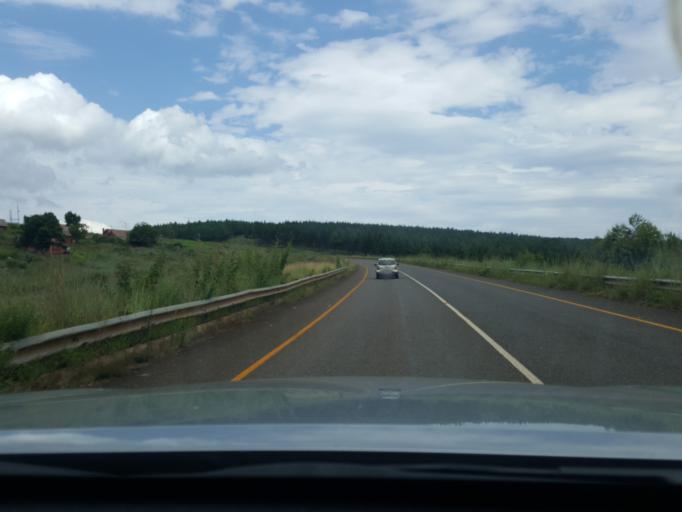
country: ZA
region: Mpumalanga
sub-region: Ehlanzeni District
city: Graksop
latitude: -25.1284
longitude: 30.8091
